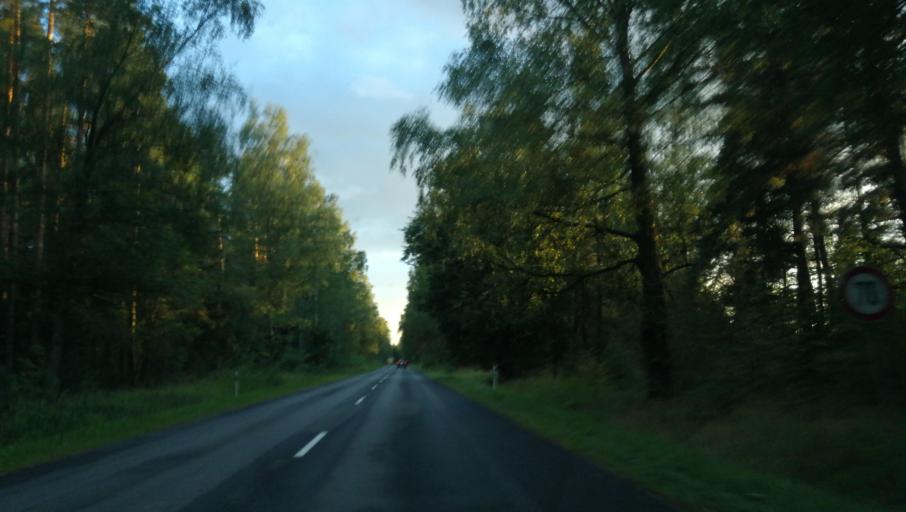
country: LV
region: Priekuli
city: Priekuli
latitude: 57.3709
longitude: 25.3868
